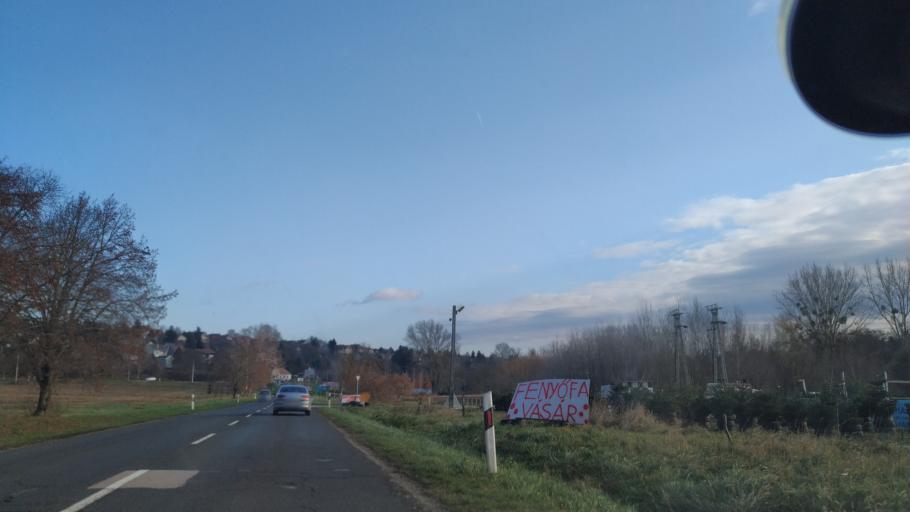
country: HU
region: Zala
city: Cserszegtomaj
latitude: 46.7926
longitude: 17.2066
